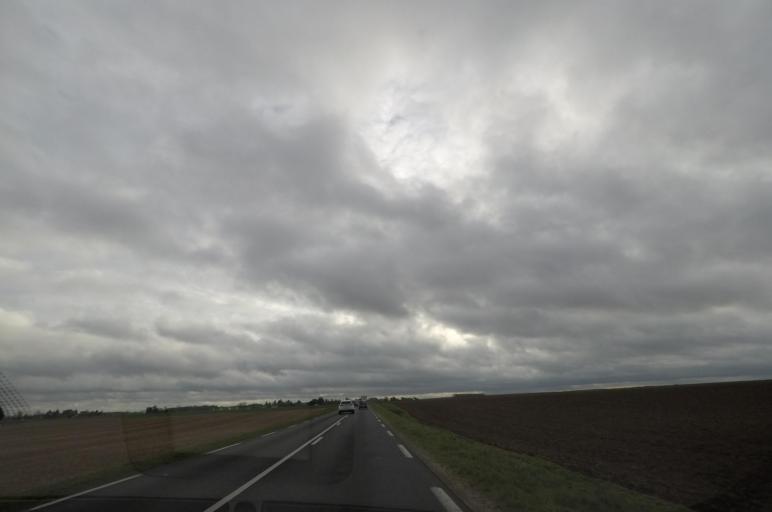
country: FR
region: Centre
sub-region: Departement du Loir-et-Cher
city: Herbault
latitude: 47.6955
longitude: 1.1845
